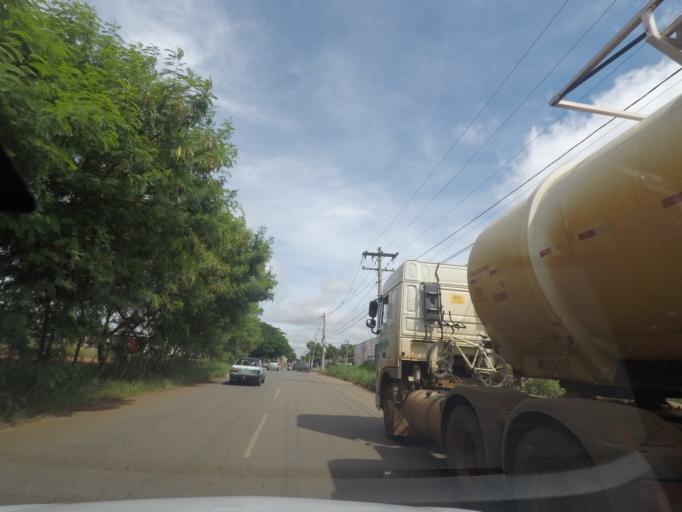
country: BR
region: Goias
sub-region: Goiania
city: Goiania
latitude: -16.6675
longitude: -49.2104
